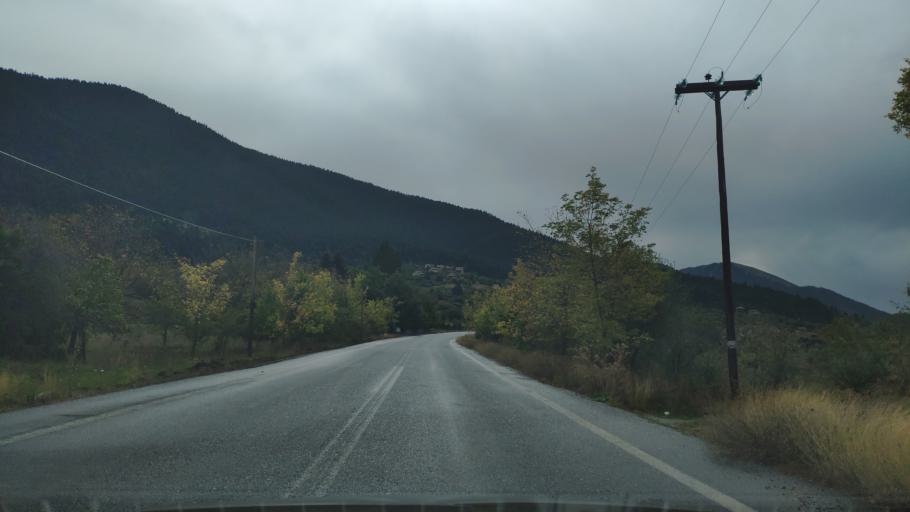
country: GR
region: Peloponnese
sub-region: Nomos Arkadias
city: Langadhia
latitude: 37.6714
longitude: 22.1936
